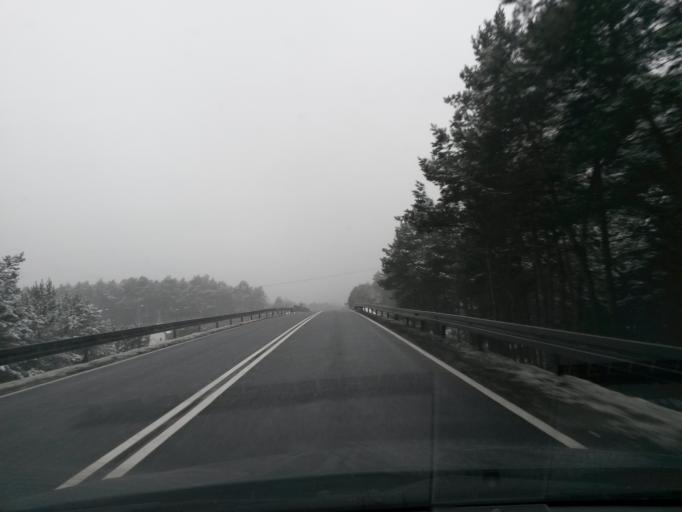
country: PL
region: Kujawsko-Pomorskie
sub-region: Powiat bydgoski
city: Nowa Wies Wielka
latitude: 53.0620
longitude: 18.0915
